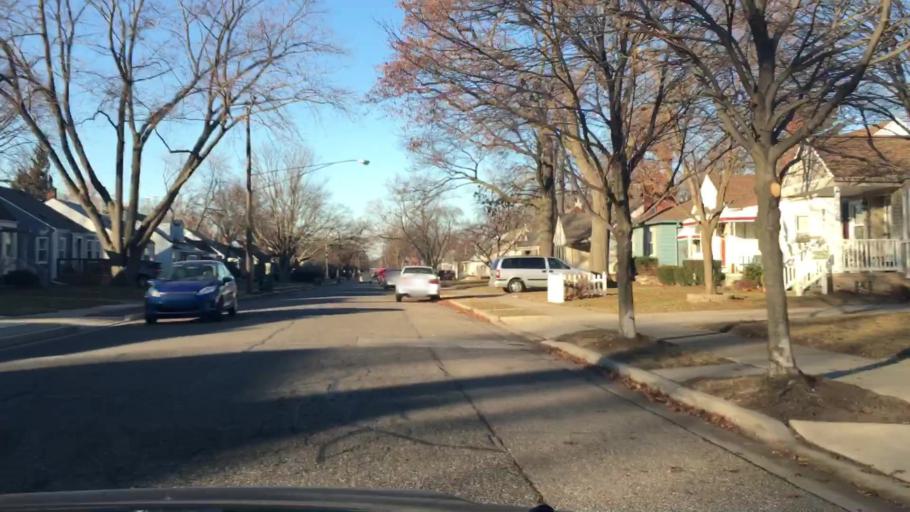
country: US
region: Michigan
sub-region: Oakland County
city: Ferndale
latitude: 42.4514
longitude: -83.1376
